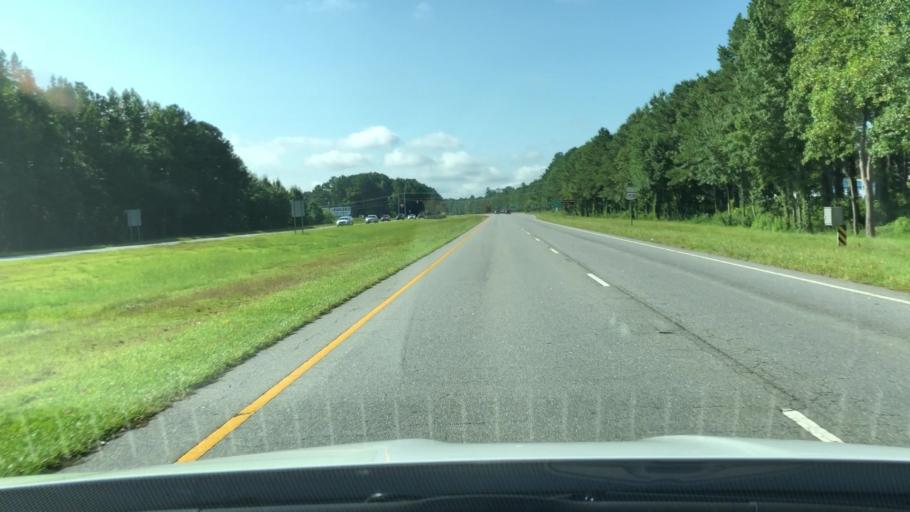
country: US
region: North Carolina
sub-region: Pasquotank County
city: Elizabeth City
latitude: 36.4175
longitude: -76.3417
